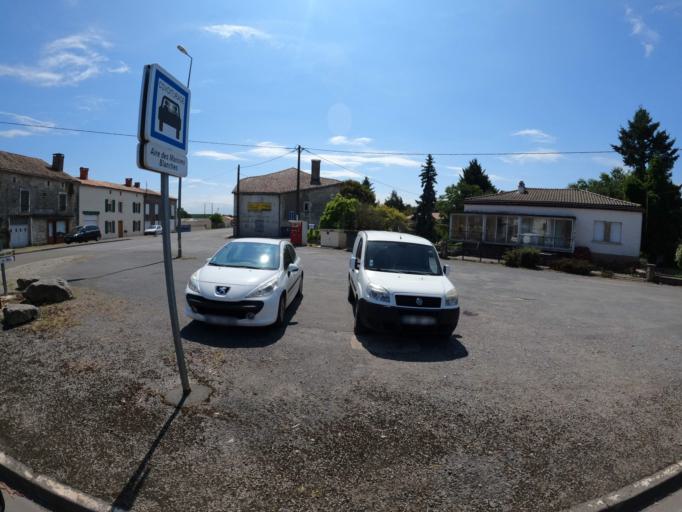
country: FR
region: Poitou-Charentes
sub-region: Departement des Deux-Sevres
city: Sauze-Vaussais
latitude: 46.1376
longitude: 0.1783
